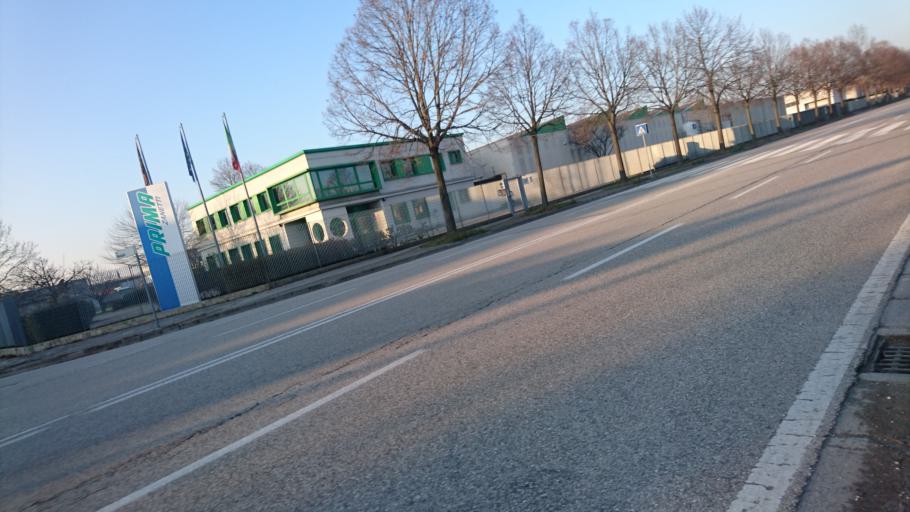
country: IT
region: Veneto
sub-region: Provincia di Padova
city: Villatora
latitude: 45.3936
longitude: 11.9527
